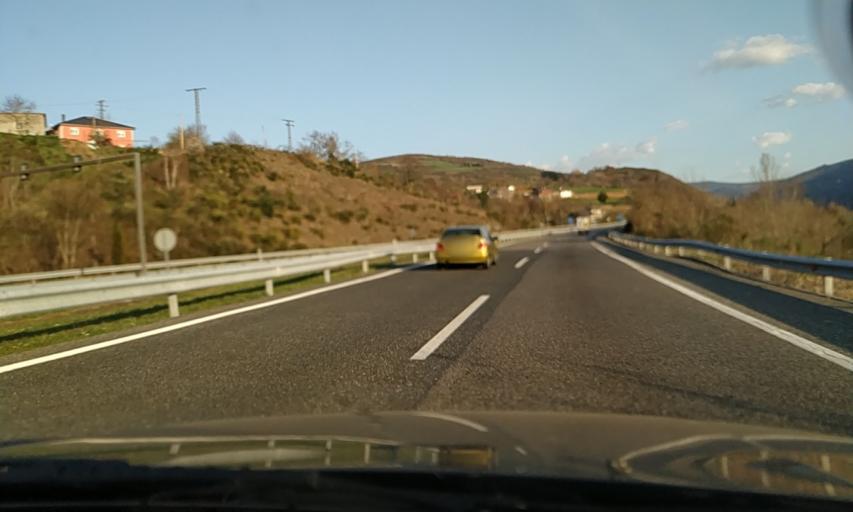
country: ES
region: Galicia
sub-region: Provincia de Lugo
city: Becerrea
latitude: 42.7832
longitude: -7.1039
